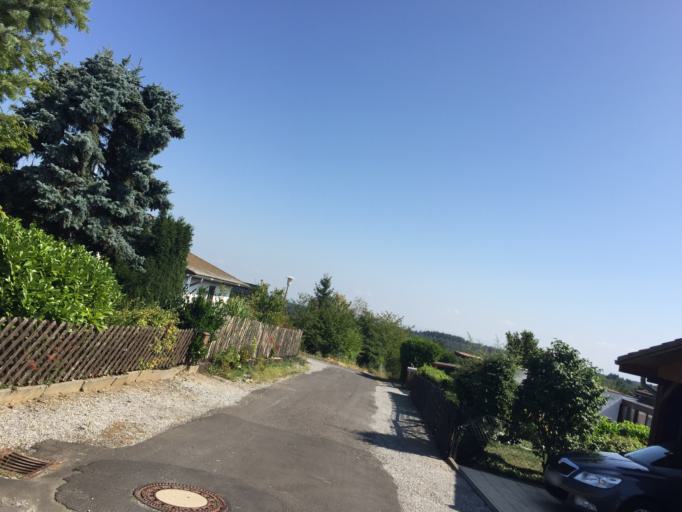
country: DE
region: Hesse
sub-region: Regierungsbezirk Darmstadt
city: Butzbach
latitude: 50.4221
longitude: 8.5901
